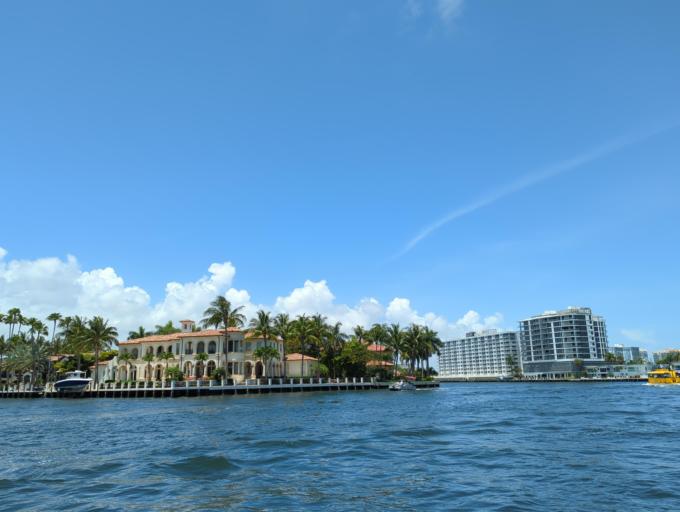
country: US
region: Florida
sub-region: Broward County
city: Sunrise
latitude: 26.1254
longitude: -80.1077
